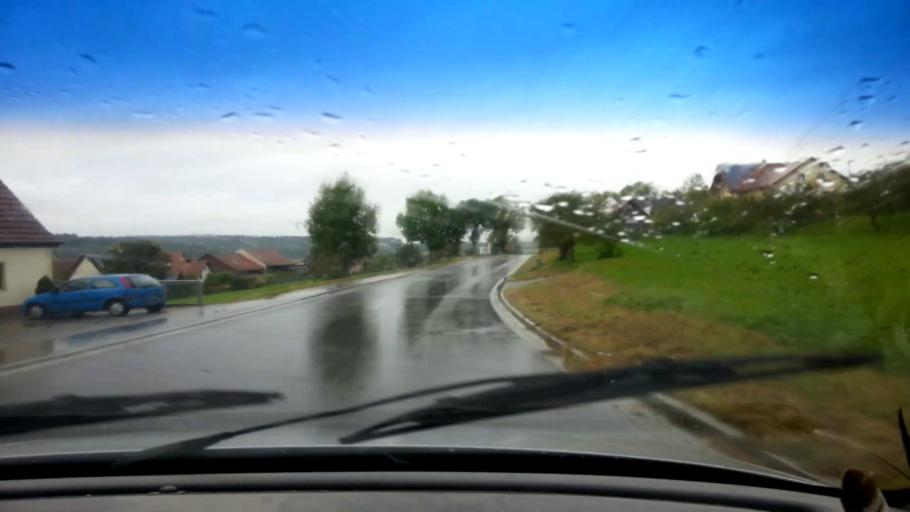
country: DE
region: Bavaria
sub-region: Upper Franconia
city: Konigsfeld
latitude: 49.9322
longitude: 11.1518
